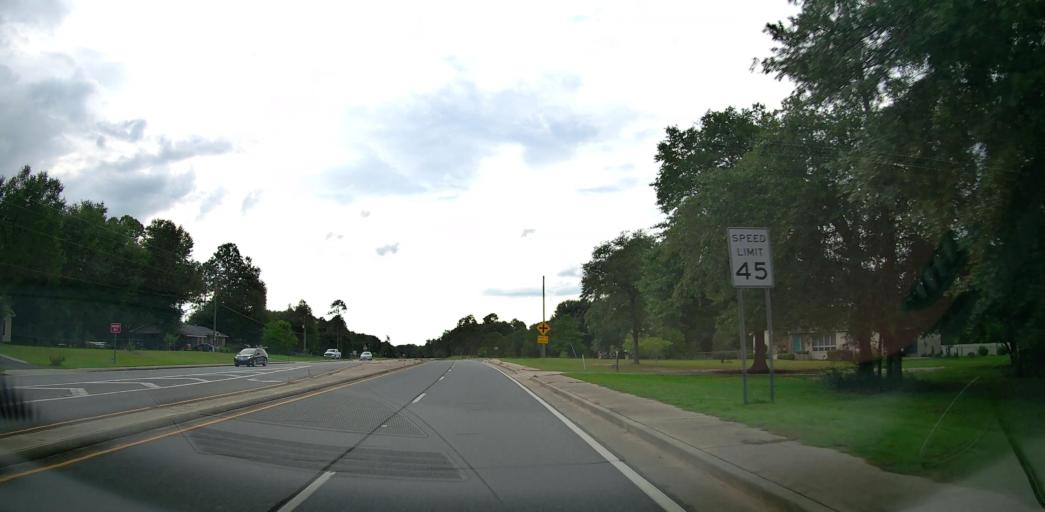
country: US
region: Georgia
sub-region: Pulaski County
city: Hawkinsville
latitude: 32.2784
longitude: -83.4275
